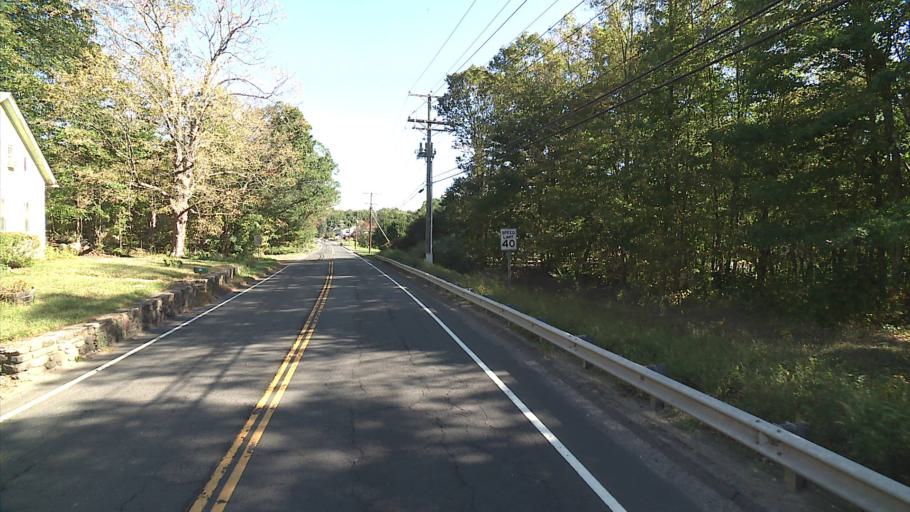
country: US
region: Connecticut
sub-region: New Haven County
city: Wolcott
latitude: 41.5801
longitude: -72.9955
